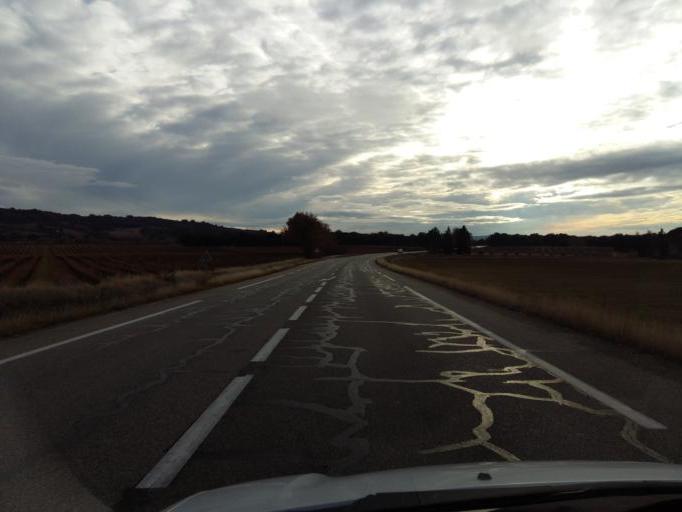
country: FR
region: Provence-Alpes-Cote d'Azur
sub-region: Departement du Vaucluse
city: Visan
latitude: 44.3466
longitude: 4.9547
